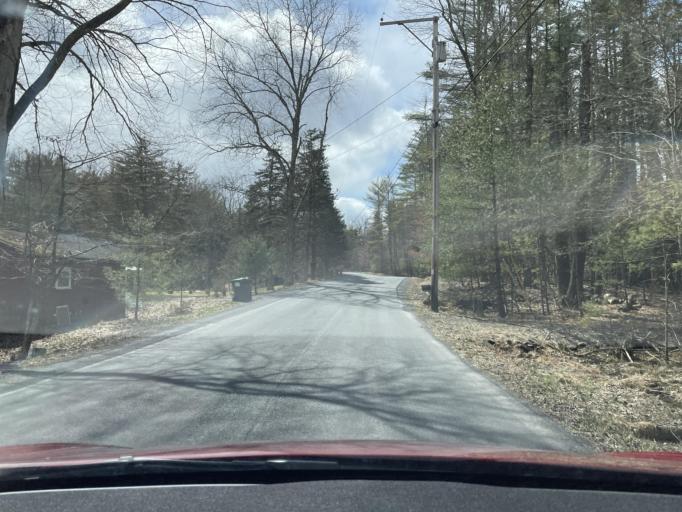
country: US
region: New York
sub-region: Ulster County
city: Zena
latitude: 42.0290
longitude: -74.0695
